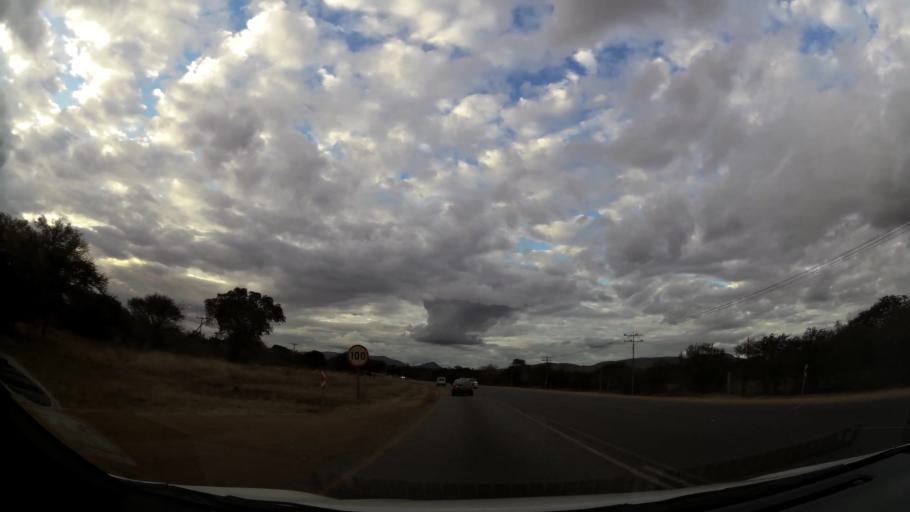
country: ZA
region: Limpopo
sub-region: Waterberg District Municipality
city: Mokopane
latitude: -24.2183
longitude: 29.0052
